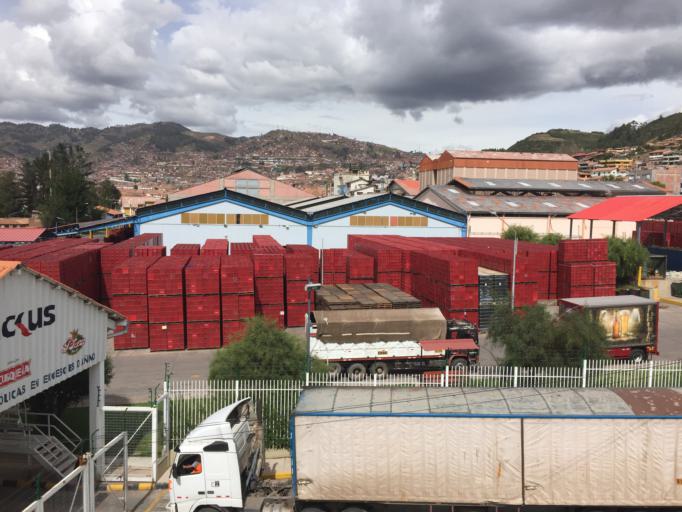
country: PE
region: Cusco
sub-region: Provincia de Cusco
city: Cusco
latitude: -13.5182
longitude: -71.9689
